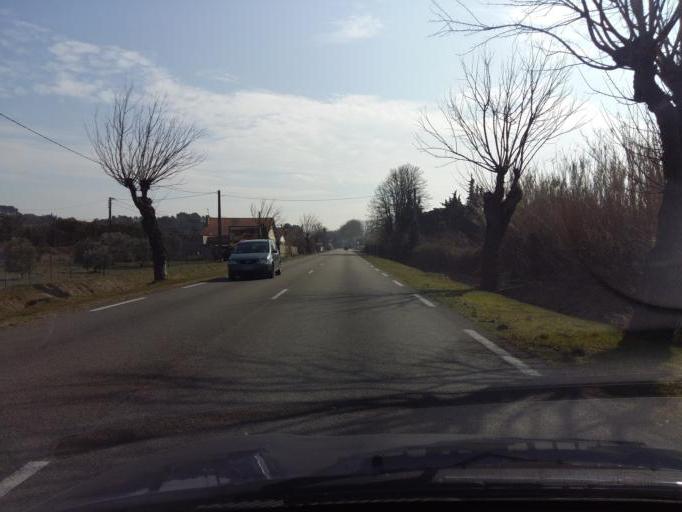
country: FR
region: Provence-Alpes-Cote d'Azur
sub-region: Departement des Bouches-du-Rhone
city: Orgon
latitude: 43.8029
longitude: 5.0023
